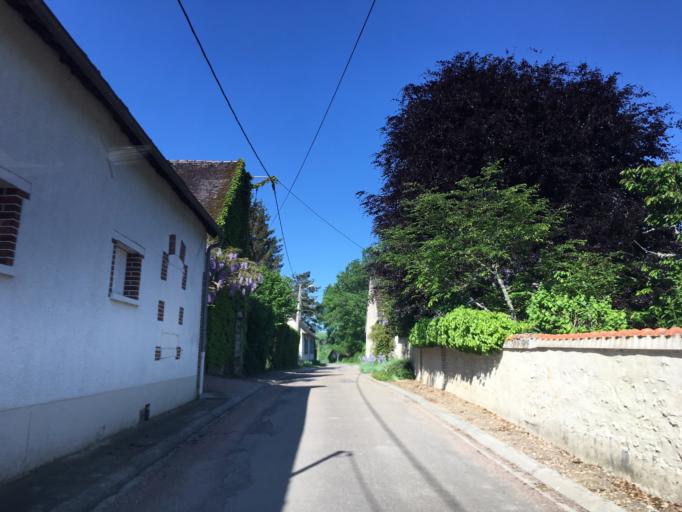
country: FR
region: Bourgogne
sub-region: Departement de l'Yonne
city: Aillant-sur-Tholon
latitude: 47.8213
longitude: 3.3493
